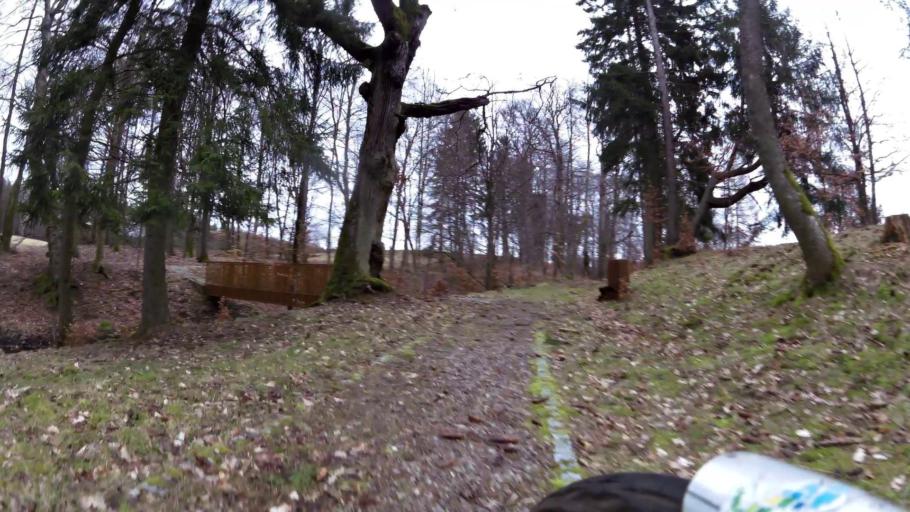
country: PL
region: Pomeranian Voivodeship
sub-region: Powiat bytowski
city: Trzebielino
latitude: 54.1411
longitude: 17.1466
